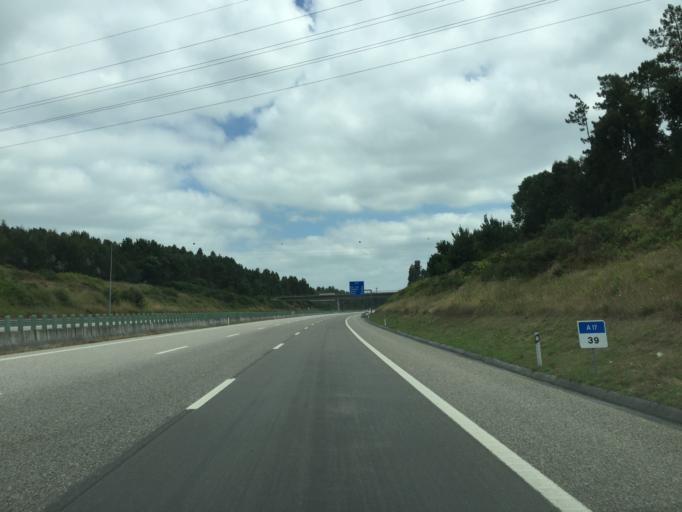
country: PT
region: Coimbra
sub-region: Figueira da Foz
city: Lavos
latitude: 40.0465
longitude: -8.8110
